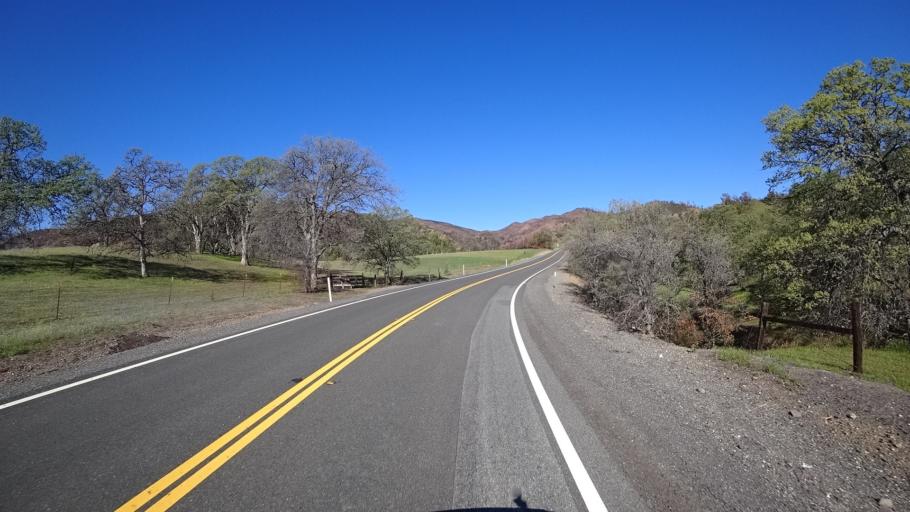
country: US
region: California
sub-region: Glenn County
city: Orland
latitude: 39.6540
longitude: -122.5862
